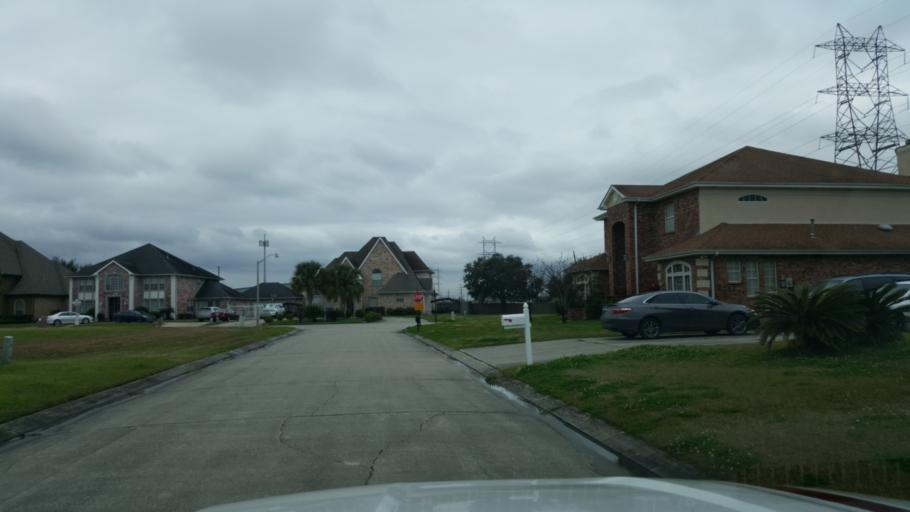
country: US
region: Louisiana
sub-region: Jefferson Parish
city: Woodmere
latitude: 29.8801
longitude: -90.0814
